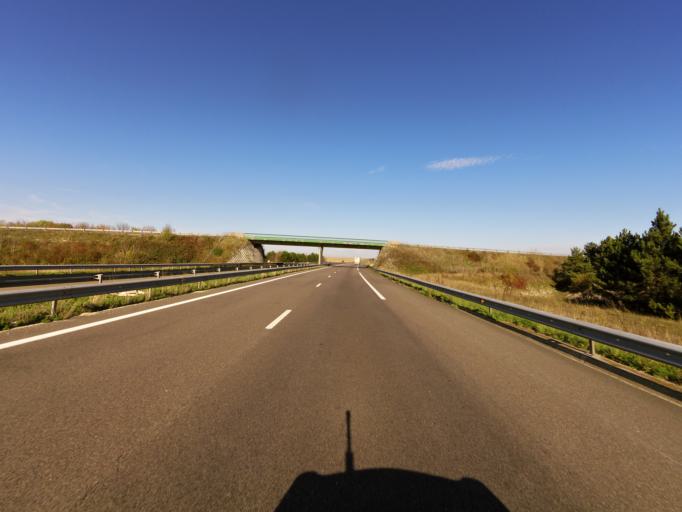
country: FR
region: Champagne-Ardenne
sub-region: Departement de la Marne
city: Fagnieres
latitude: 49.0307
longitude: 4.2840
